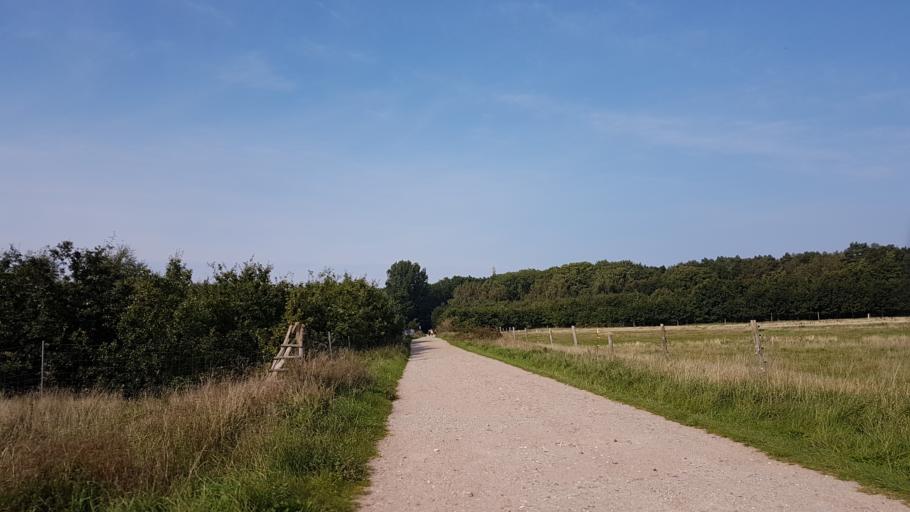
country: DE
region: Mecklenburg-Vorpommern
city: Glowe
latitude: 54.5587
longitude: 13.4625
